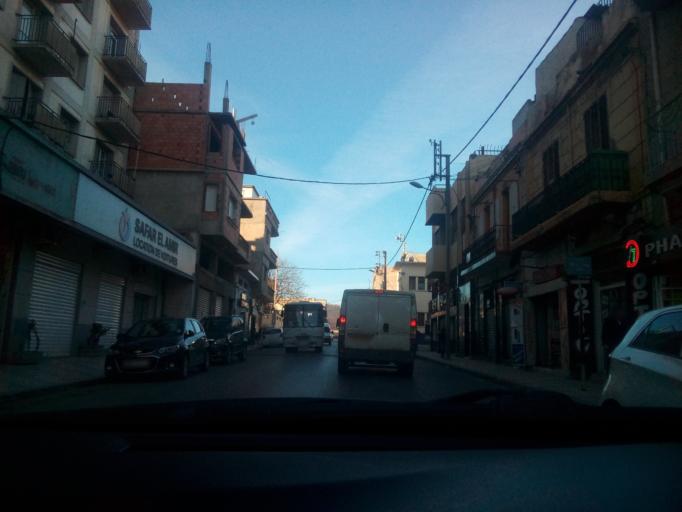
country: DZ
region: Oran
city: Oran
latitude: 35.6888
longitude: -0.6617
